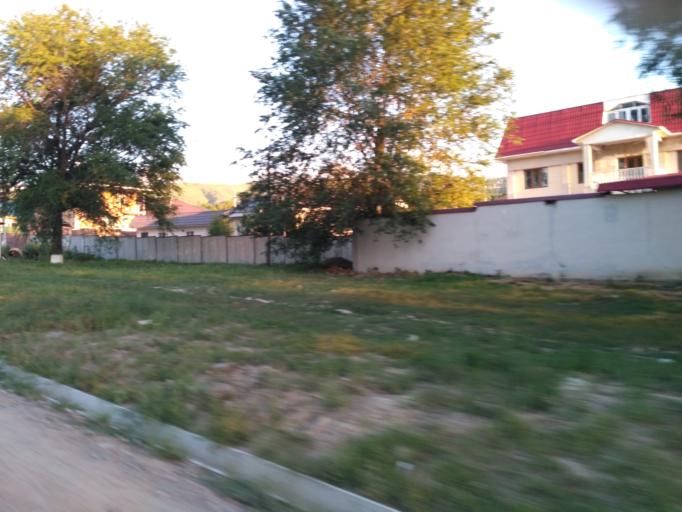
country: KZ
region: Almaty Qalasy
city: Almaty
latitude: 43.1715
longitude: 76.7722
